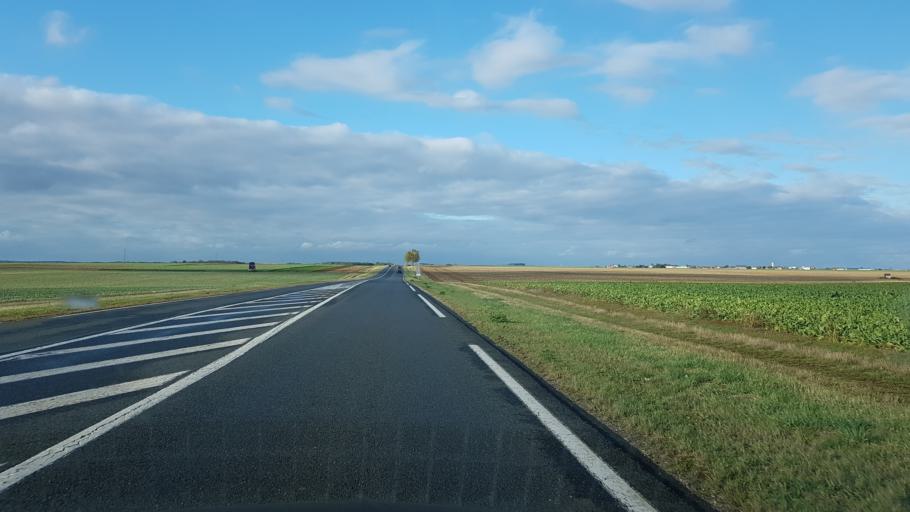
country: FR
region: Centre
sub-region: Departement du Loiret
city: Sermaises
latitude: 48.3040
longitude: 2.2007
